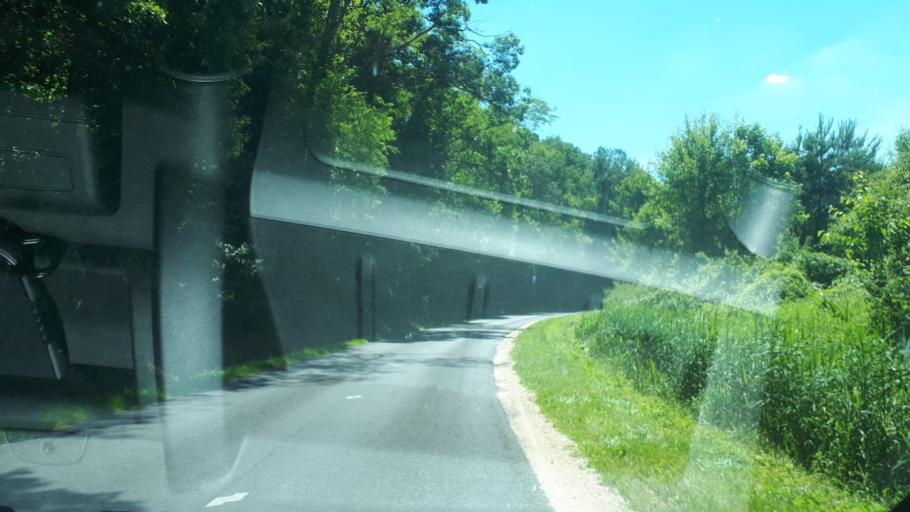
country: FR
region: Centre
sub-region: Departement du Loir-et-Cher
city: Chouzy-sur-Cisse
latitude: 47.5704
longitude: 1.2194
